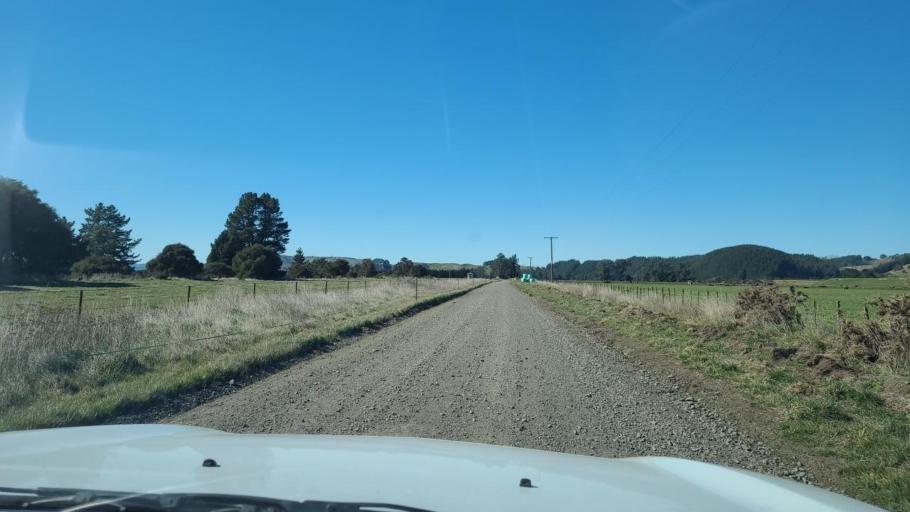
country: NZ
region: Hawke's Bay
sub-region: Napier City
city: Taradale
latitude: -39.4616
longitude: 176.5804
